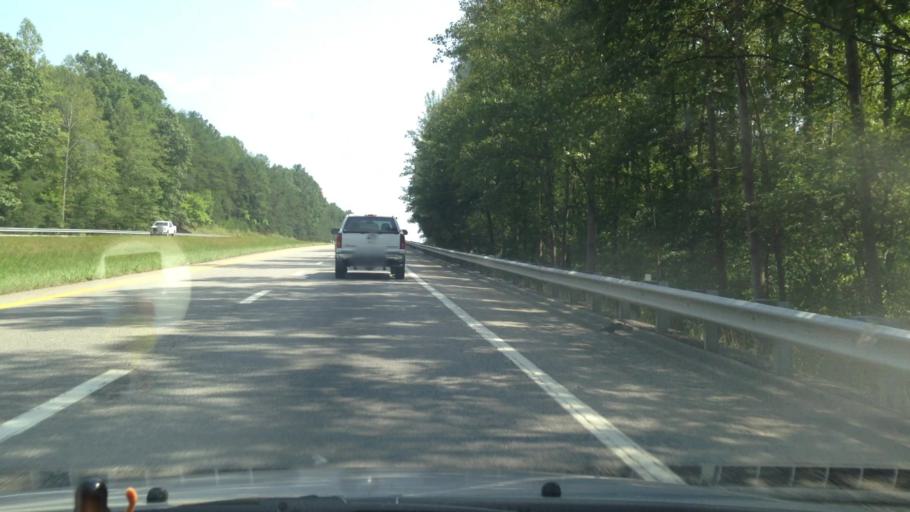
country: US
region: Virginia
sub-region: Henry County
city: Collinsville
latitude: 36.6785
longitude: -79.9351
